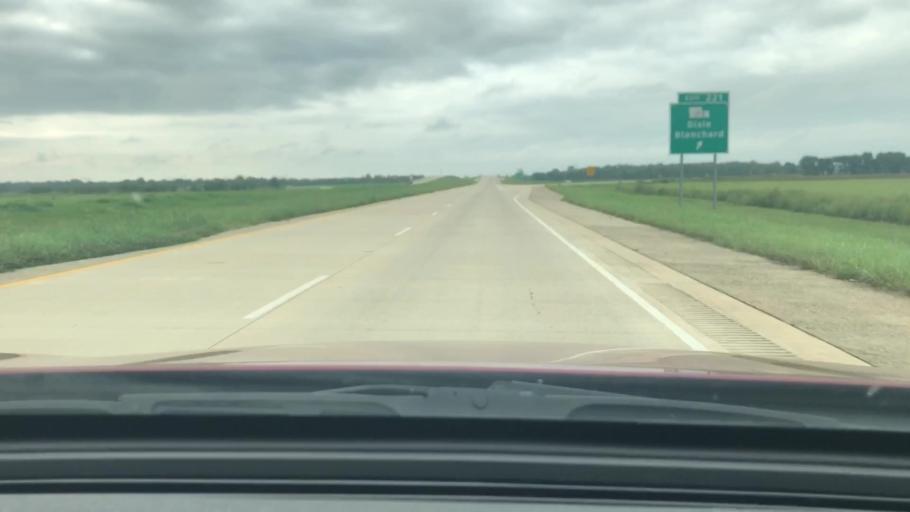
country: US
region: Louisiana
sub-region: Caddo Parish
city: Blanchard
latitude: 32.6798
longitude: -93.8527
